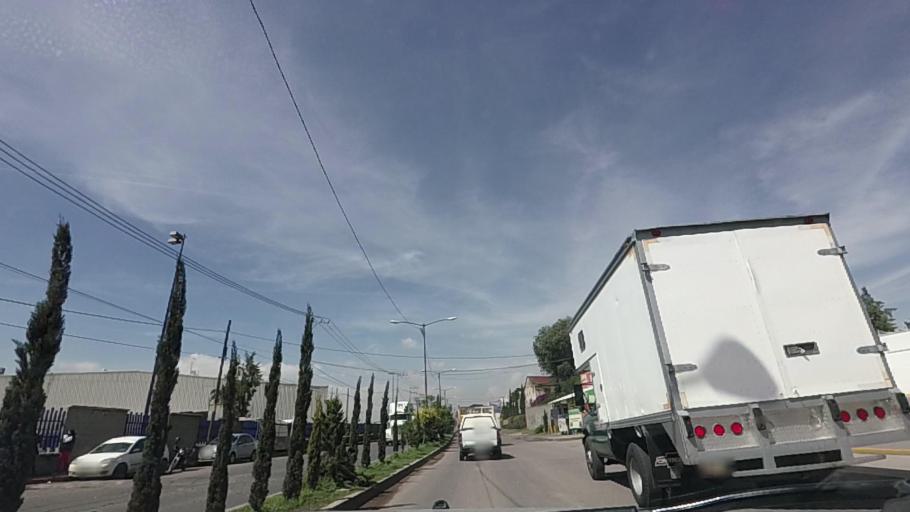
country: MX
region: Mexico
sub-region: Cuautitlan
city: San Jose del Puente
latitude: 19.7192
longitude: -99.1925
